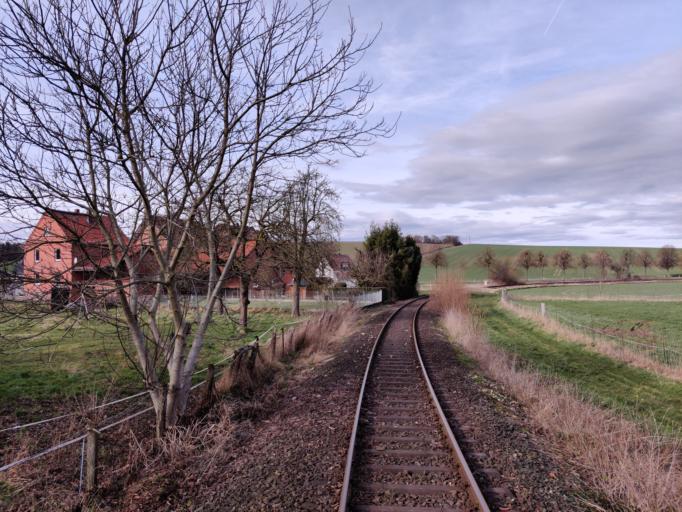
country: DE
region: Lower Saxony
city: Bockenem
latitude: 51.9847
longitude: 10.1159
